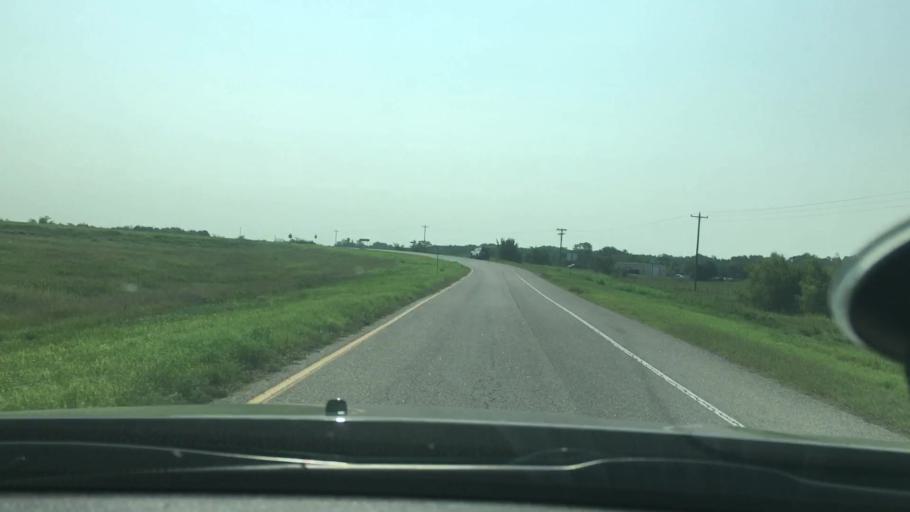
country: US
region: Oklahoma
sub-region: Pontotoc County
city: Ada
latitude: 34.6414
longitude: -96.5325
